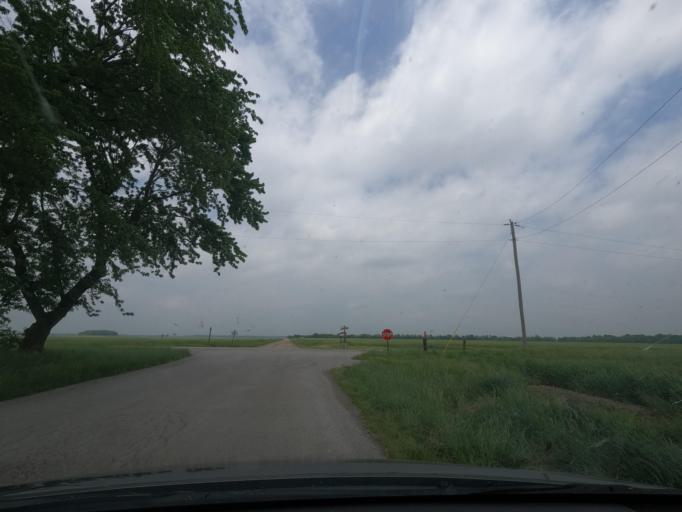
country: US
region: Kansas
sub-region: Cherokee County
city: Columbus
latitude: 37.2816
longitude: -94.9406
